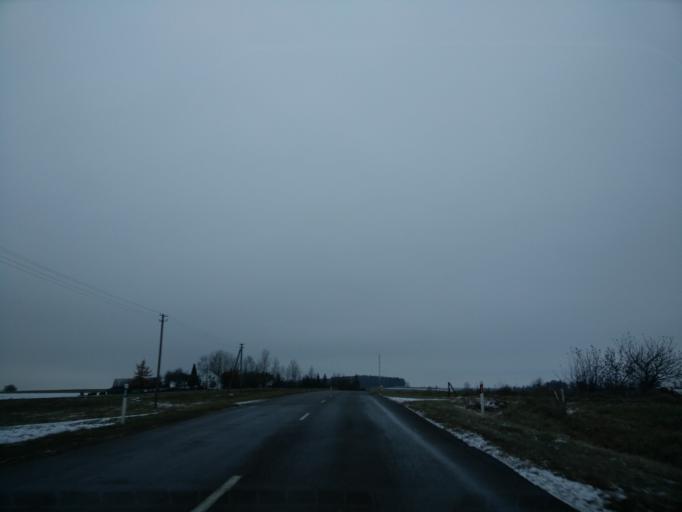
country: LT
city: Ariogala
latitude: 55.3380
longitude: 23.4000
